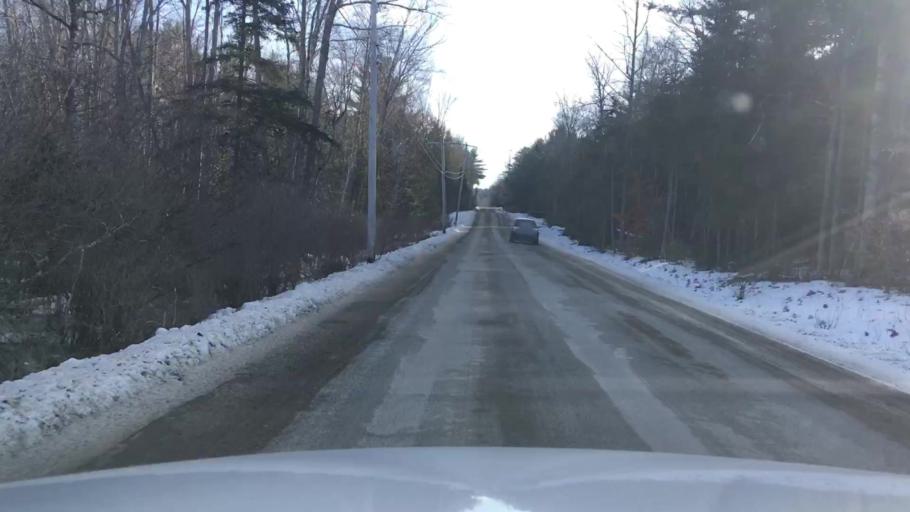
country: US
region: Maine
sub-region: Penobscot County
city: Holden
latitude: 44.7739
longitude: -68.5847
